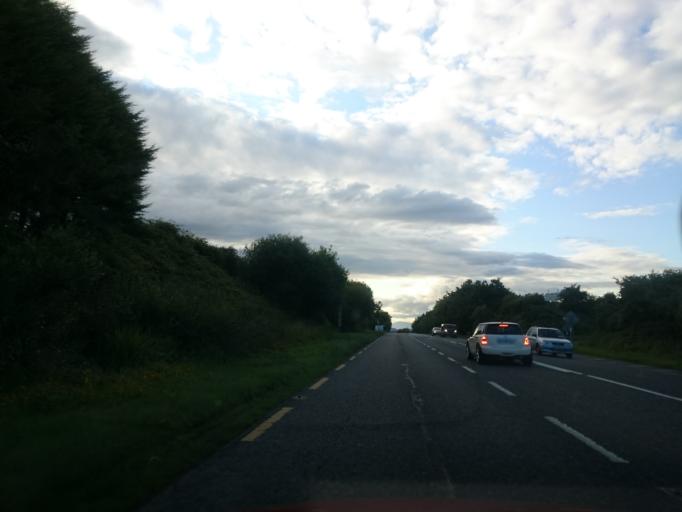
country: IE
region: Leinster
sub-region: Loch Garman
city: Loch Garman
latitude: 52.3254
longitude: -6.5036
